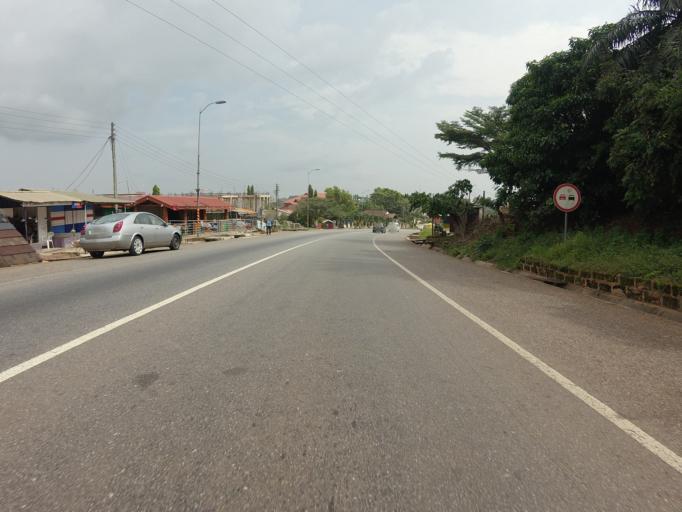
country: GH
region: Eastern
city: Aburi
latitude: 5.8123
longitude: -0.1853
